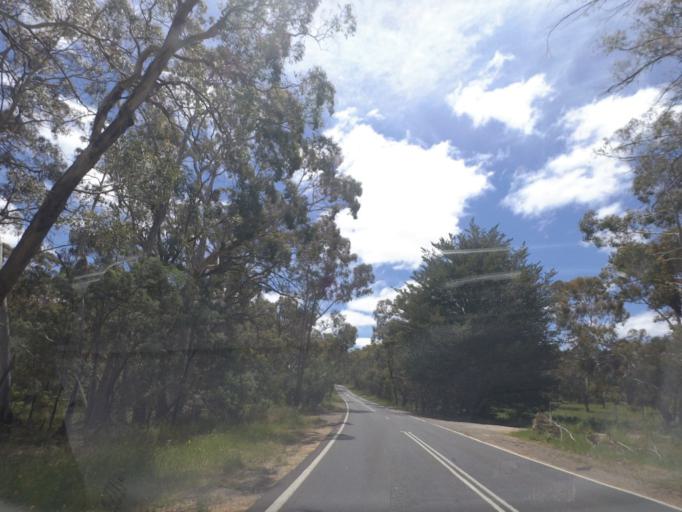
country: AU
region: Victoria
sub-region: Mount Alexander
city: Castlemaine
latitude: -37.3133
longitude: 144.1664
